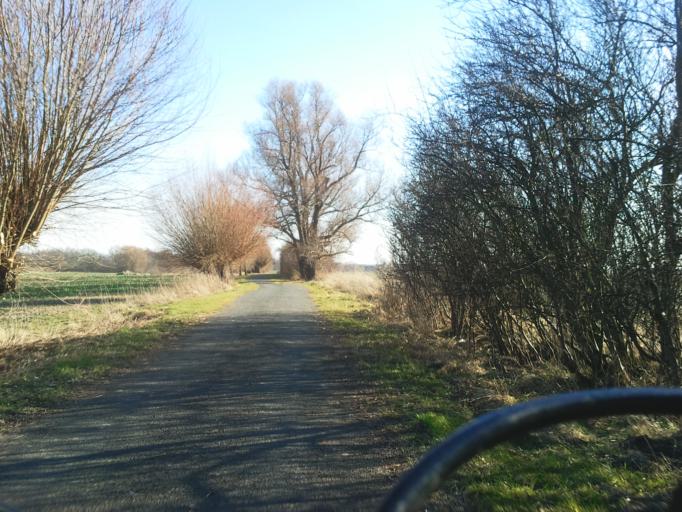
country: DE
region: Mecklenburg-Vorpommern
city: Dierkow-West
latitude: 54.1281
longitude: 12.1274
